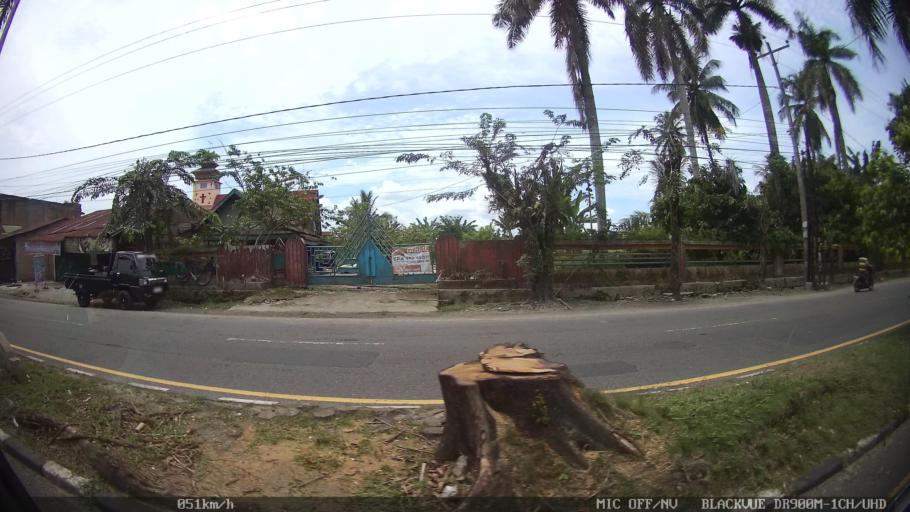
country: ID
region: North Sumatra
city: Sunggal
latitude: 3.5231
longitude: 98.6269
